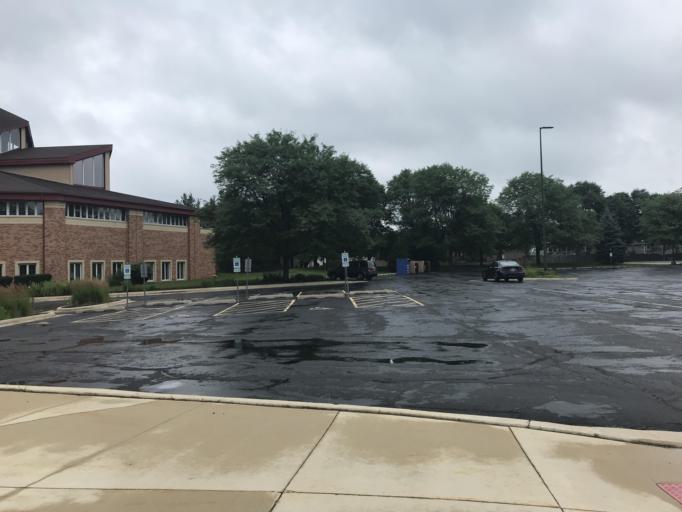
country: US
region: Illinois
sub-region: Will County
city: Bolingbrook
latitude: 41.7264
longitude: -88.1005
